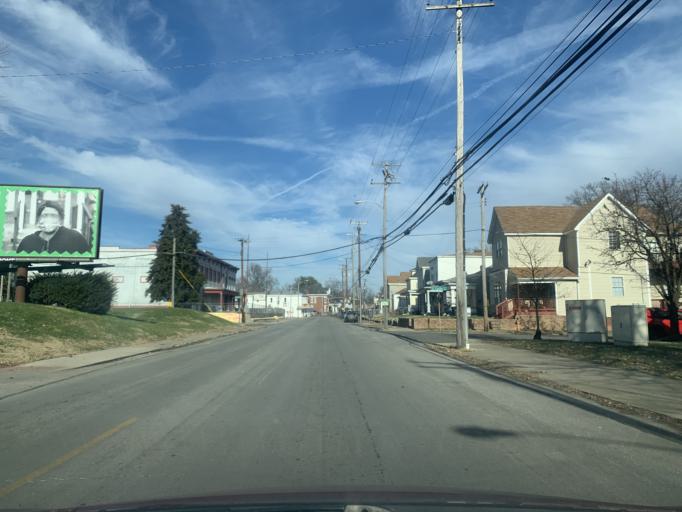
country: US
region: Kentucky
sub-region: Jefferson County
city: Louisville
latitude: 38.2643
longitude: -85.7931
